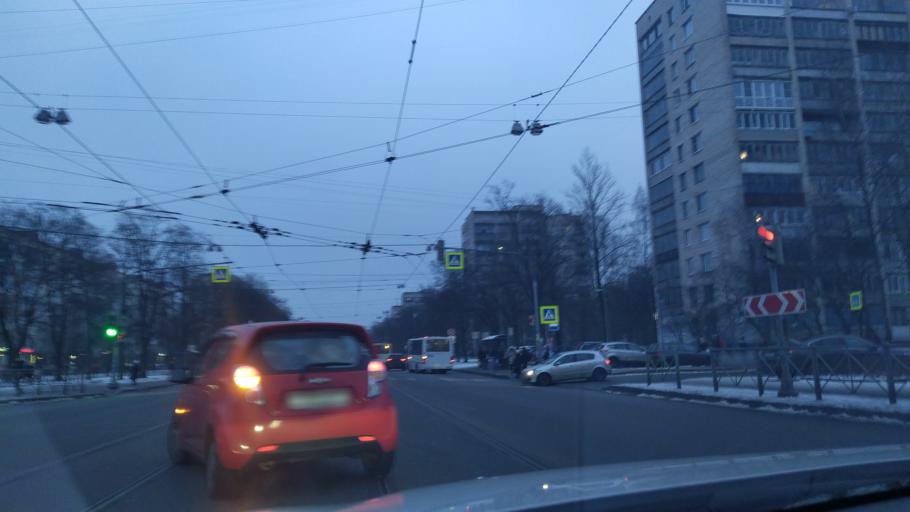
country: RU
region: Leningrad
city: Akademicheskoe
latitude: 60.0104
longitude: 30.4082
